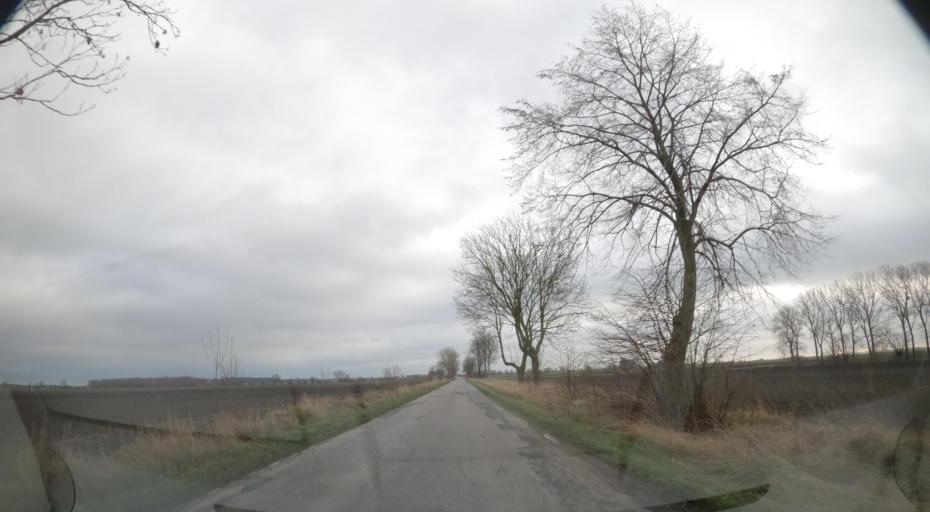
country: PL
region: Greater Poland Voivodeship
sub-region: Powiat pilski
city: Lobzenica
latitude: 53.2668
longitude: 17.2085
